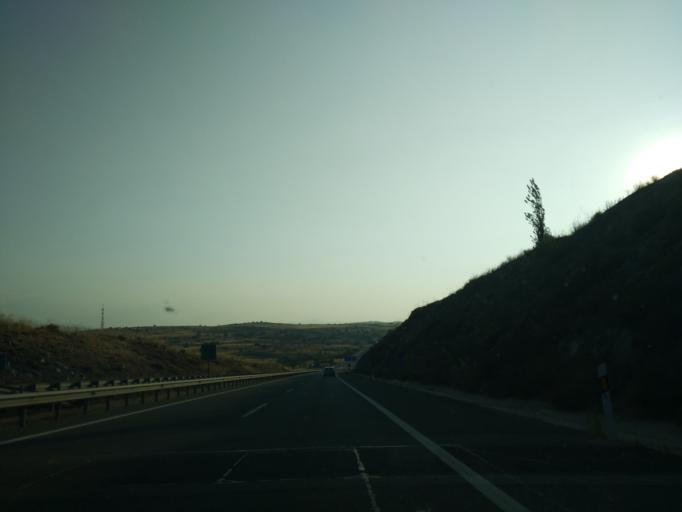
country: ES
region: Castille and Leon
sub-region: Provincia de Avila
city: Avila
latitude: 40.6730
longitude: -4.7034
